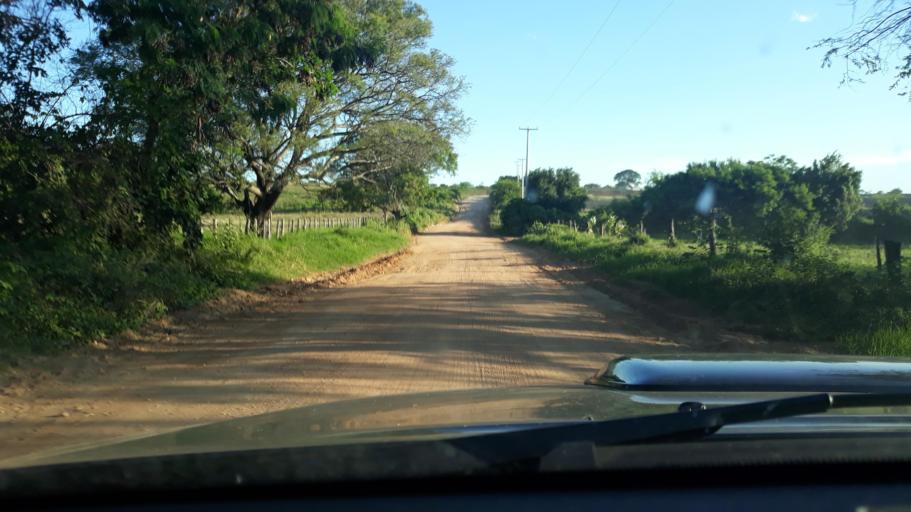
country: BR
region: Bahia
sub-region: Riacho De Santana
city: Riacho de Santana
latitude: -13.7887
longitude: -42.7127
